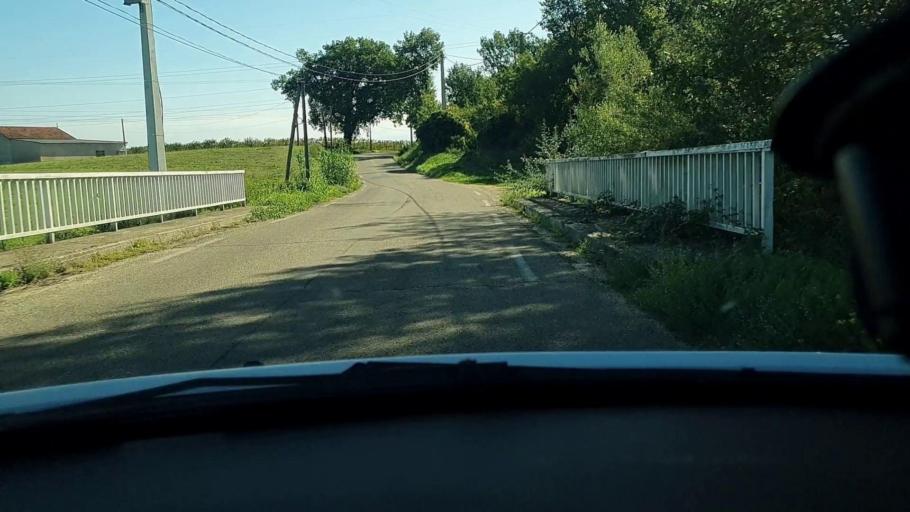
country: FR
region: Languedoc-Roussillon
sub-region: Departement du Gard
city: Saint-Paulet-de-Caisson
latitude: 44.2657
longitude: 4.5797
